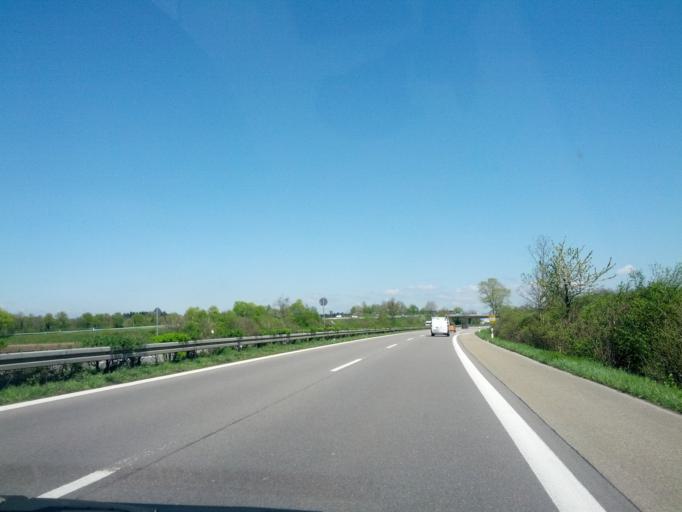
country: DE
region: Baden-Wuerttemberg
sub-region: Freiburg Region
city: Ebringen
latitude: 47.9773
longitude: 7.7740
